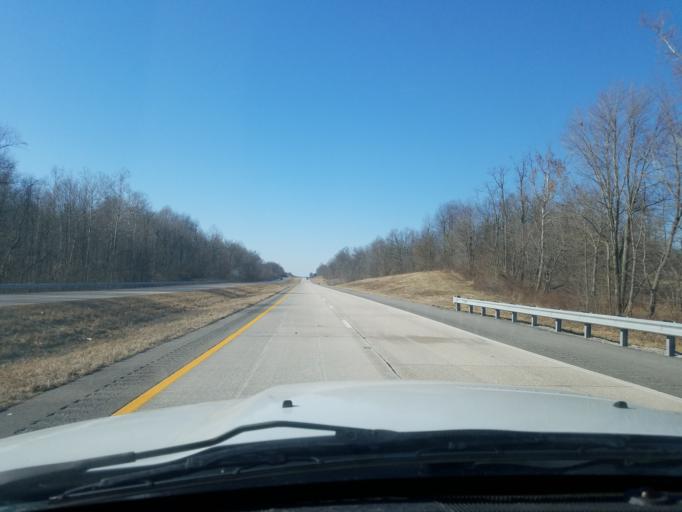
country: US
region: Kentucky
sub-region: Henderson County
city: Henderson
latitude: 37.7756
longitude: -87.4399
